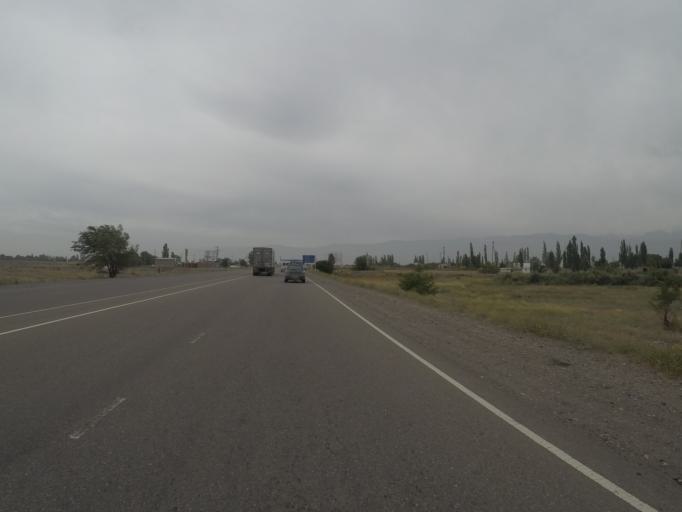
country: KG
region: Chuy
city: Bystrovka
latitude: 42.8258
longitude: 75.5430
